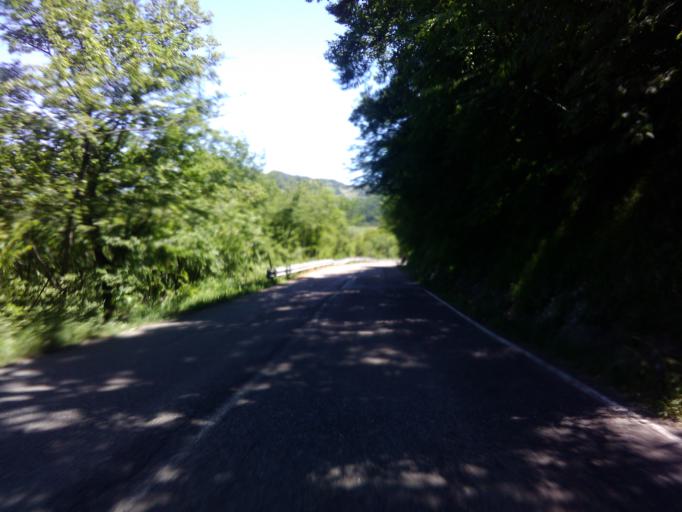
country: IT
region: Emilia-Romagna
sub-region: Provincia di Parma
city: Terenzo
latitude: 44.5820
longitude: 10.0810
